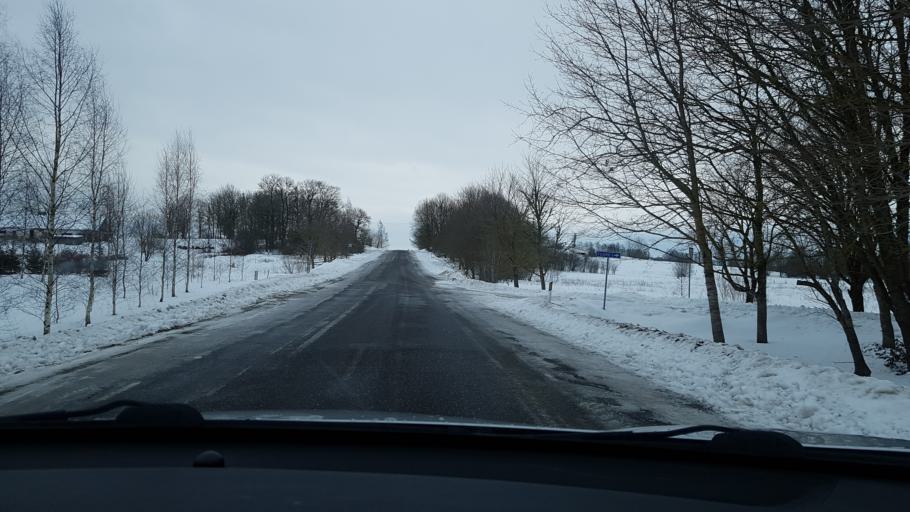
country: EE
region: Jaervamaa
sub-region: Koeru vald
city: Koeru
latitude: 58.9832
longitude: 25.9885
